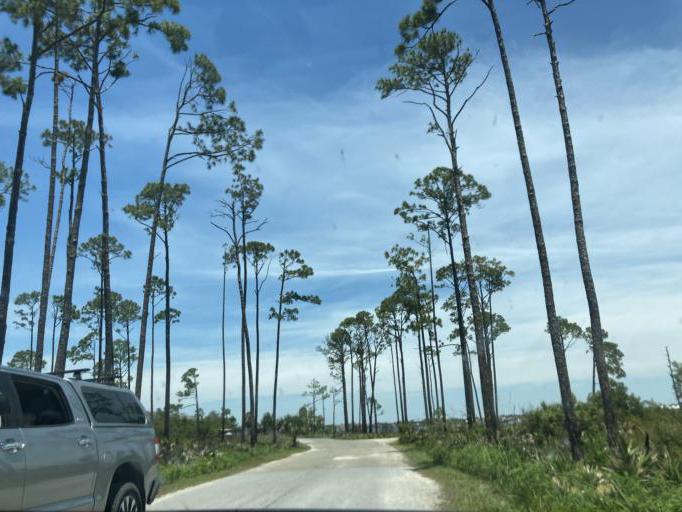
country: US
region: Florida
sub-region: Bay County
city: Lower Grand Lagoon
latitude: 30.1327
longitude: -85.7324
